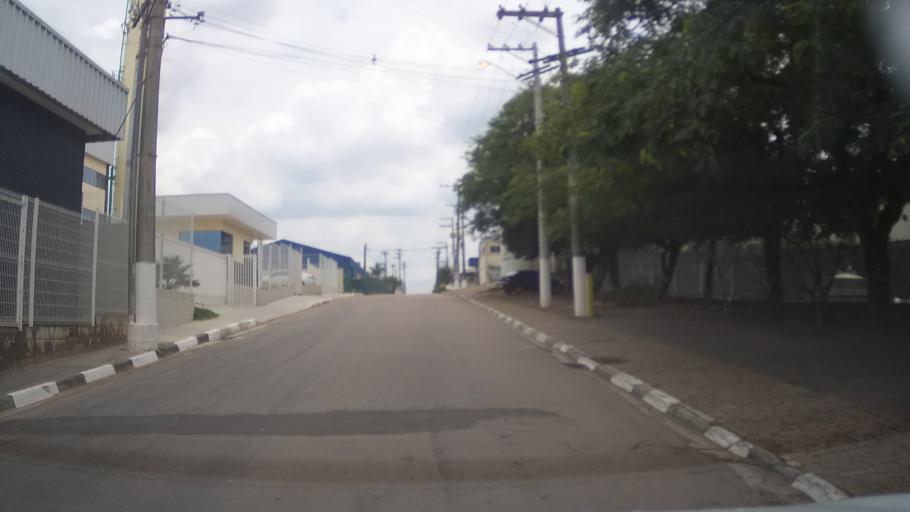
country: BR
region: Sao Paulo
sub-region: Itupeva
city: Itupeva
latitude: -23.1571
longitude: -47.0355
